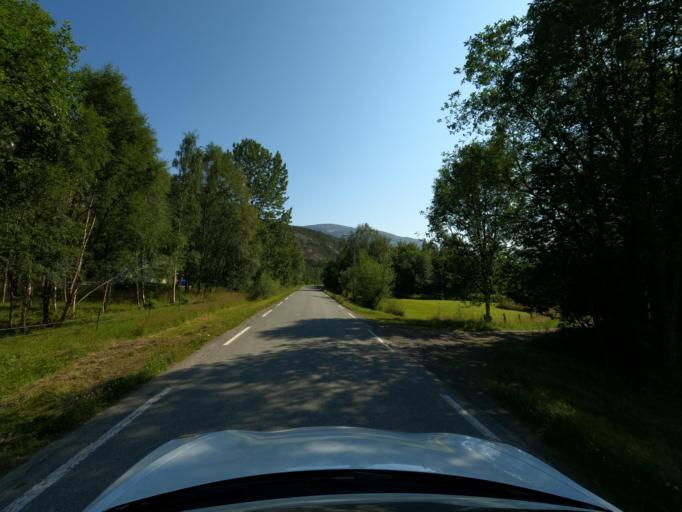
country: NO
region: Nordland
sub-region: Narvik
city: Narvik
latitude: 68.1875
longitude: 17.5531
